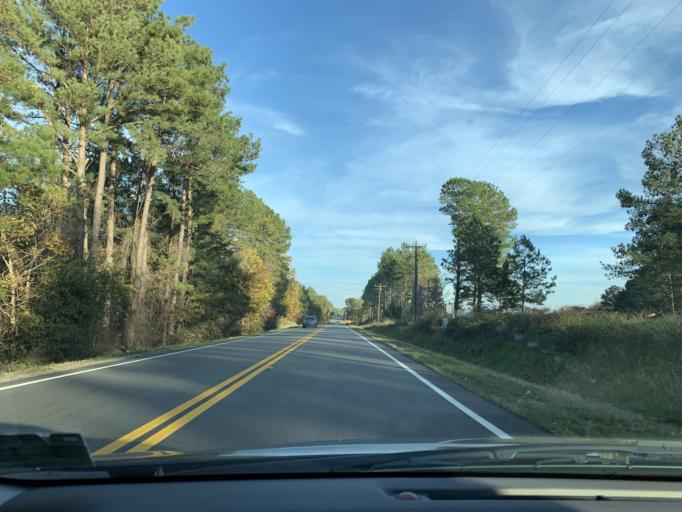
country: US
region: Georgia
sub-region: Irwin County
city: Ocilla
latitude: 31.5956
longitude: -83.1378
